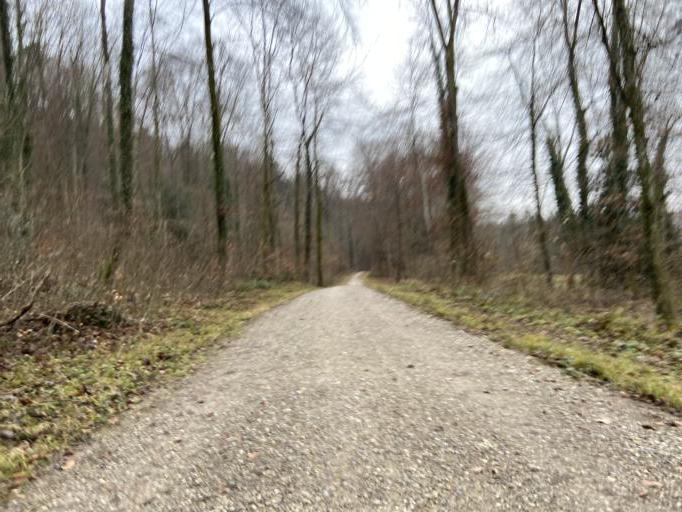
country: CH
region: Zurich
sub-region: Bezirk Winterthur
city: Toess (Kreis 4) / Vorder-Daettnau
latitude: 47.4861
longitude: 8.6858
